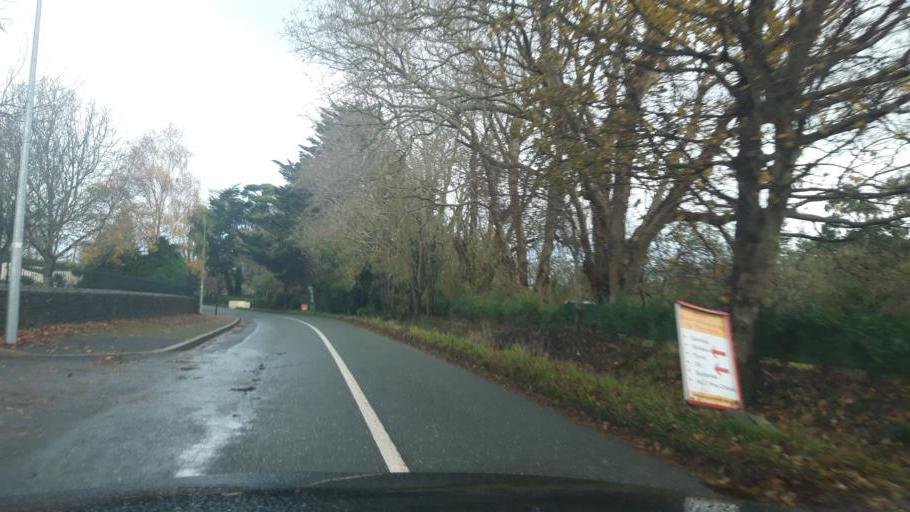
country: IE
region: Leinster
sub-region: Wicklow
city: Kilcoole
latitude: 53.0943
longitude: -6.0676
